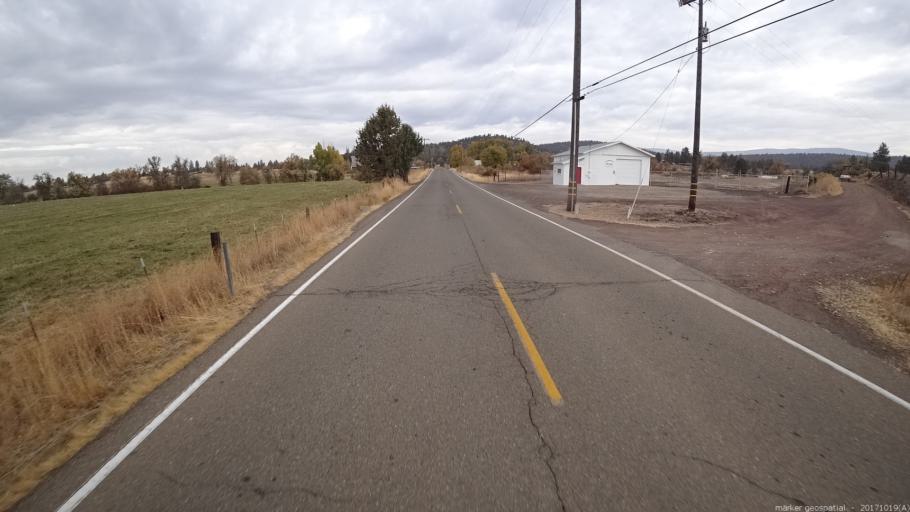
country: US
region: California
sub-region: Shasta County
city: Burney
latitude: 41.0437
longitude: -121.3314
